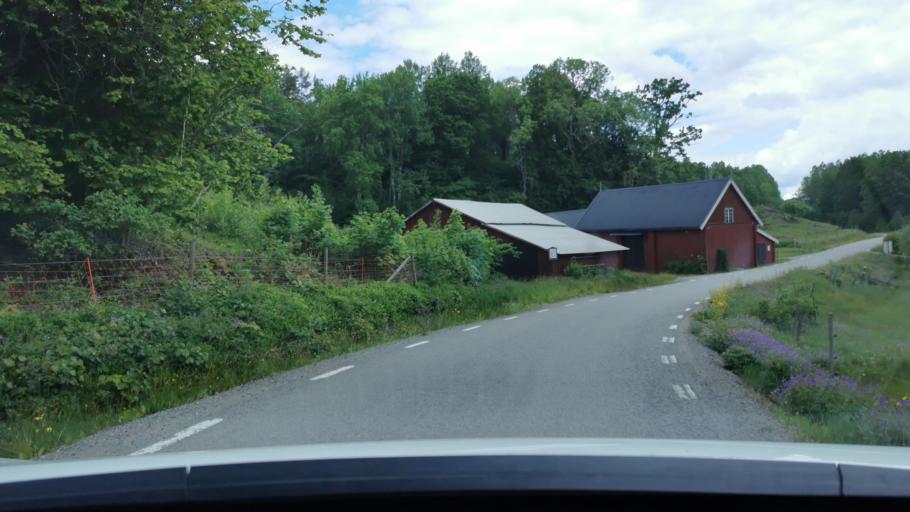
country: SE
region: Vaestra Goetaland
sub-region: Bengtsfors Kommun
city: Dals Langed
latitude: 58.8356
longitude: 12.3294
